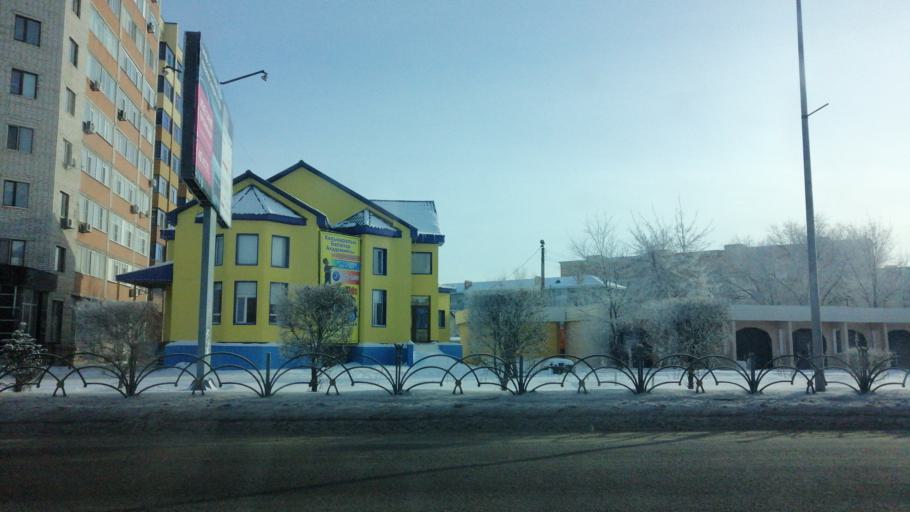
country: KZ
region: Aqtoebe
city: Aqtobe
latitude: 50.2919
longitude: 57.1674
